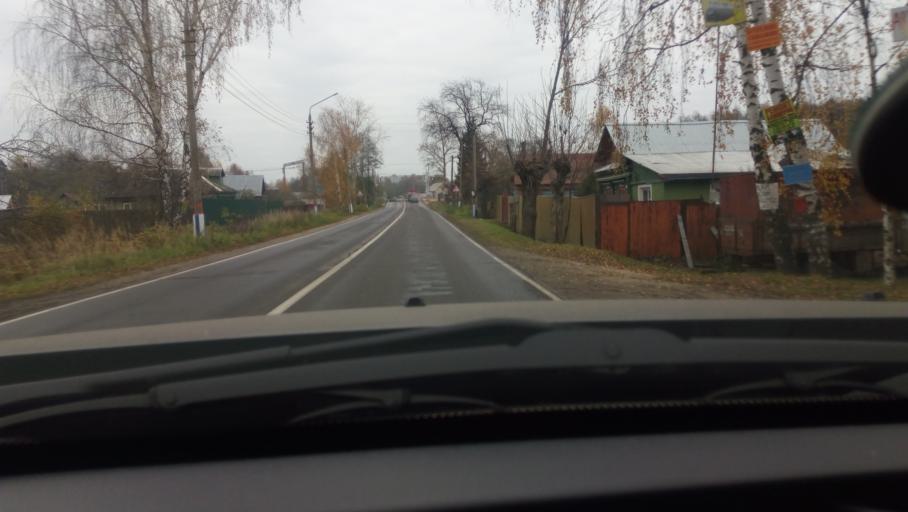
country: RU
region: Moskovskaya
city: Likino-Dulevo
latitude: 55.7010
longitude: 38.9425
